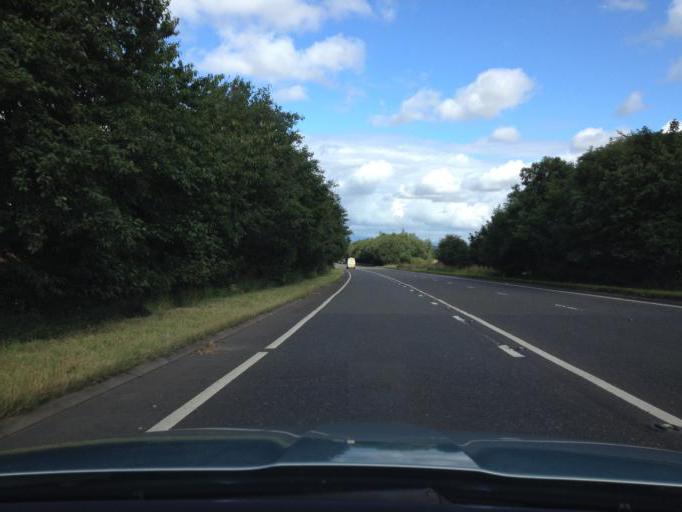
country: GB
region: Scotland
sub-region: West Lothian
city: Bathgate
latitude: 55.9097
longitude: -3.6748
